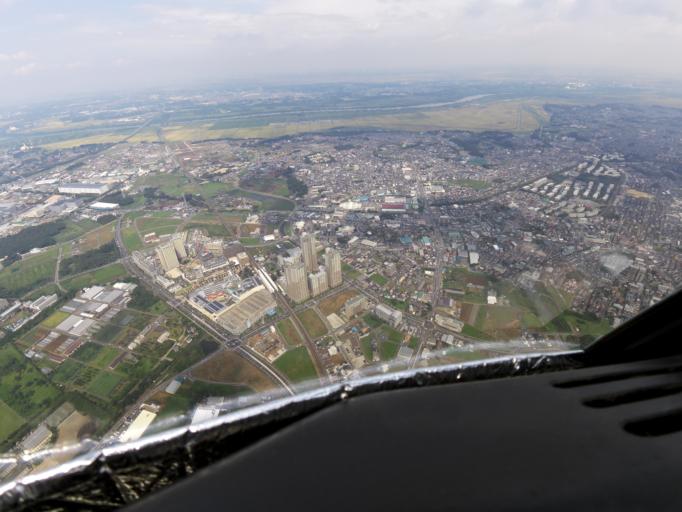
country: JP
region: Chiba
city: Kashiwa
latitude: 35.8863
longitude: 139.9478
